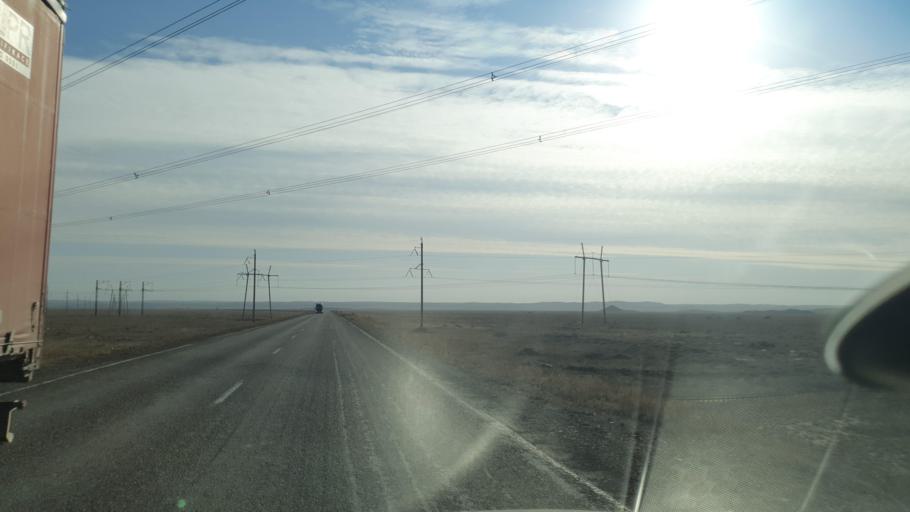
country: KZ
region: Zhambyl
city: Mynaral
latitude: 45.6003
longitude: 73.3993
